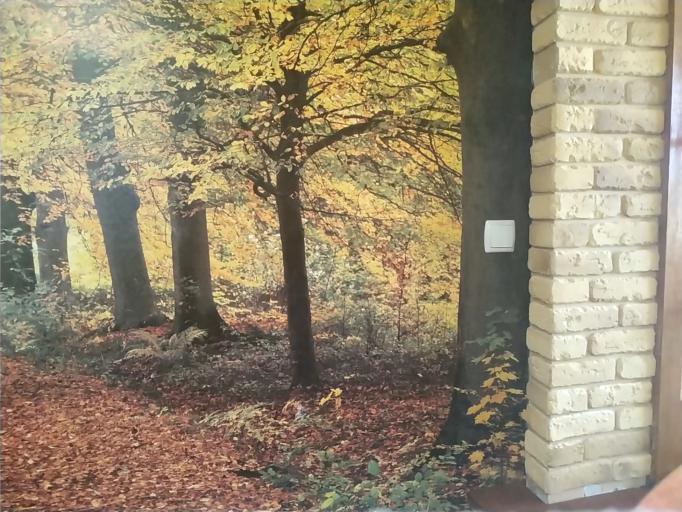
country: RU
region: Tverskaya
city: Vyshniy Volochek
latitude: 57.6808
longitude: 34.5176
